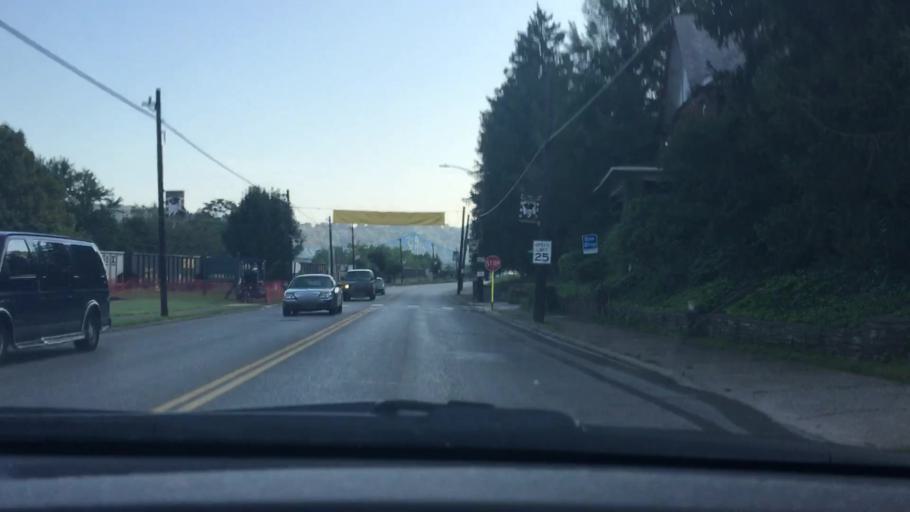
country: US
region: Pennsylvania
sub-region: Allegheny County
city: Dravosburg
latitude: 40.3397
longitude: -79.8882
